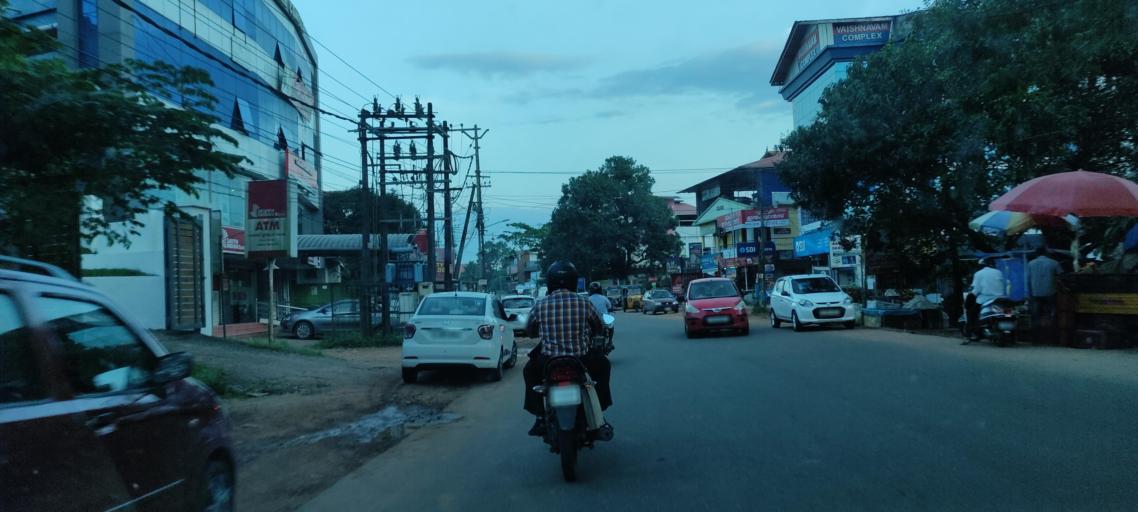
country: IN
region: Kerala
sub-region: Pattanamtitta
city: Adur
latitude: 9.1592
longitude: 76.7247
